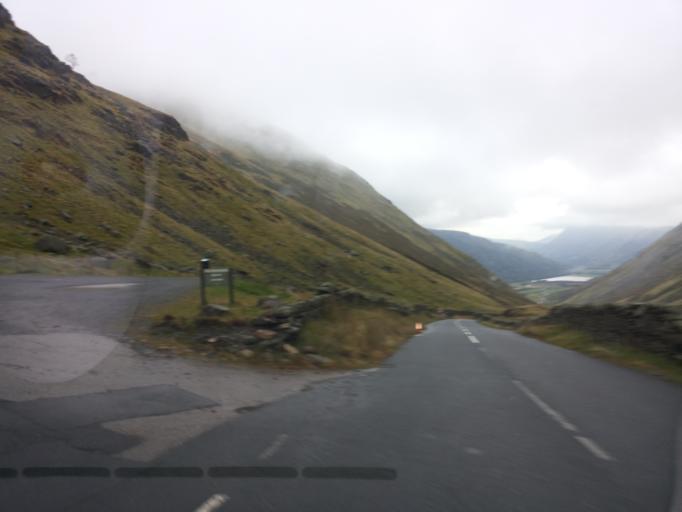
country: GB
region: England
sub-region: Cumbria
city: Ambleside
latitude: 54.4721
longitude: -2.9227
